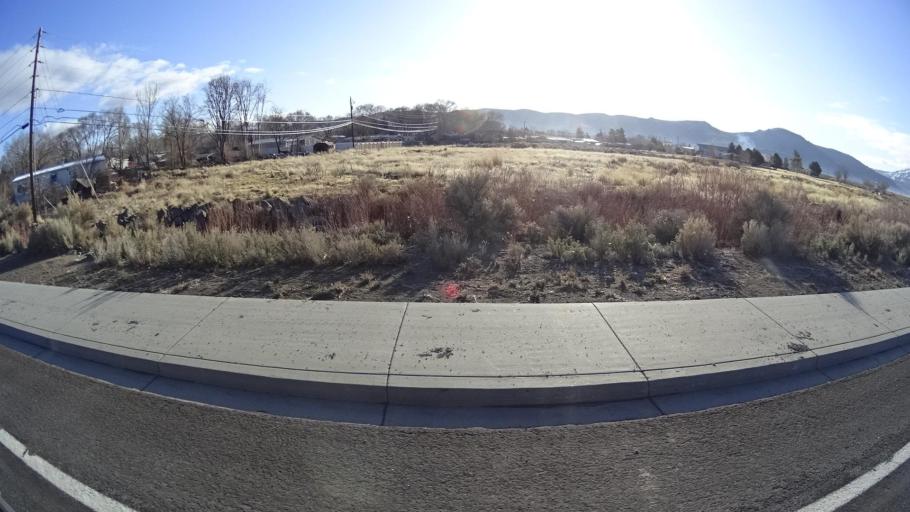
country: US
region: Nevada
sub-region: Washoe County
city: Cold Springs
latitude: 39.6775
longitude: -119.9787
